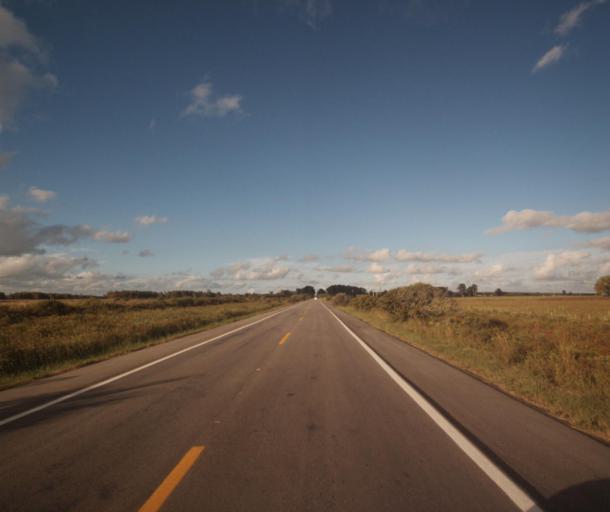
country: BR
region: Rio Grande do Sul
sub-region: Rio Grande
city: Rio Grande
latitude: -32.1300
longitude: -52.3694
